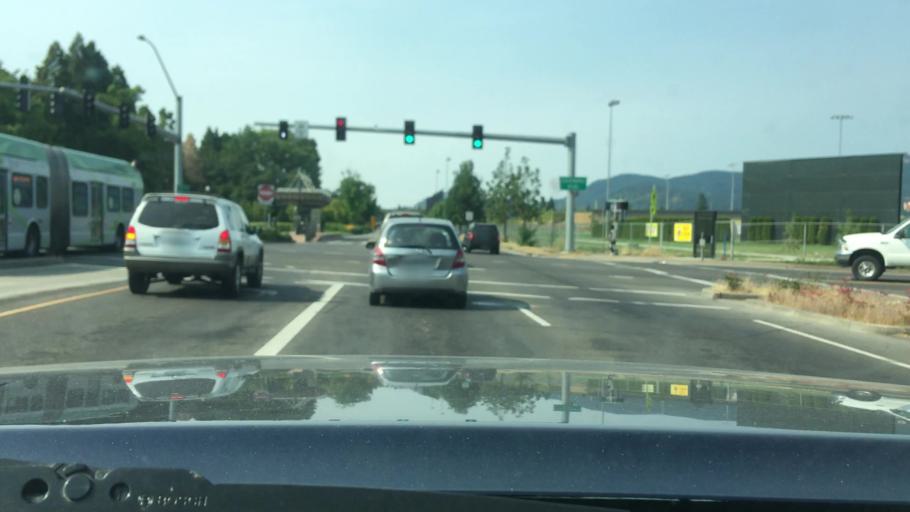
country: US
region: Oregon
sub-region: Lane County
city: Springfield
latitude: 44.0564
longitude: -123.0238
